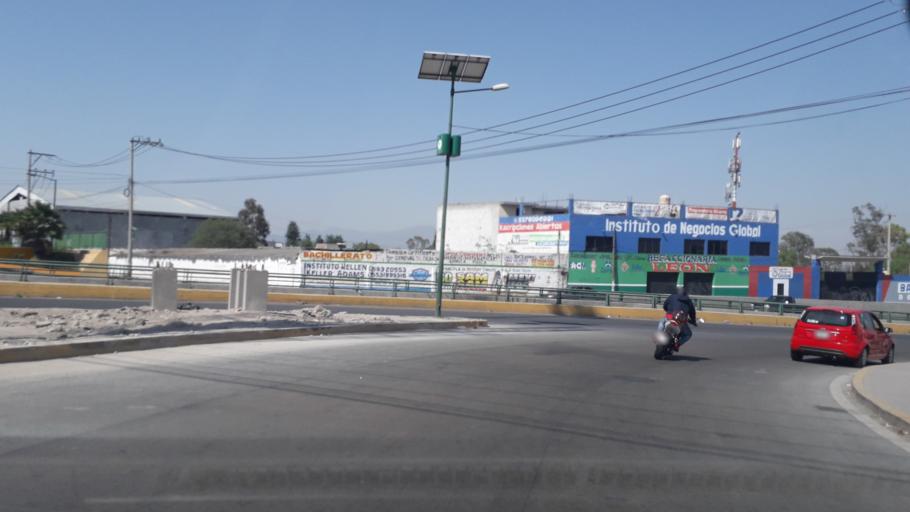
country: MX
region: Mexico
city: Santo Tomas Chiconautla
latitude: 19.6601
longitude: -99.0048
